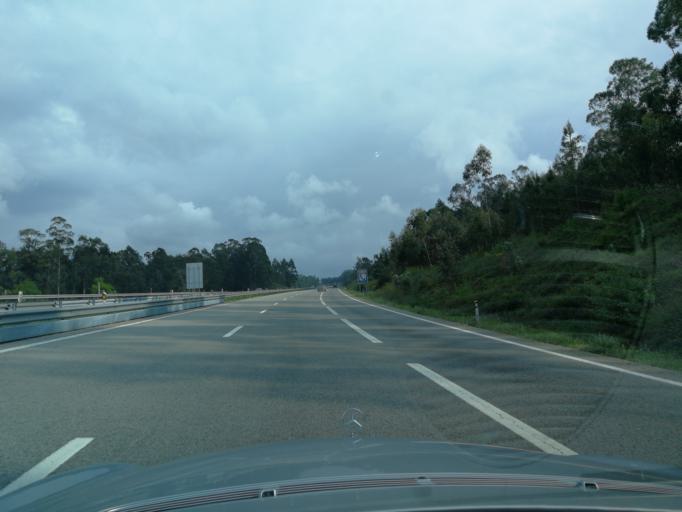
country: PT
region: Porto
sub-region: Vila do Conde
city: Arvore
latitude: 41.3904
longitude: -8.6730
